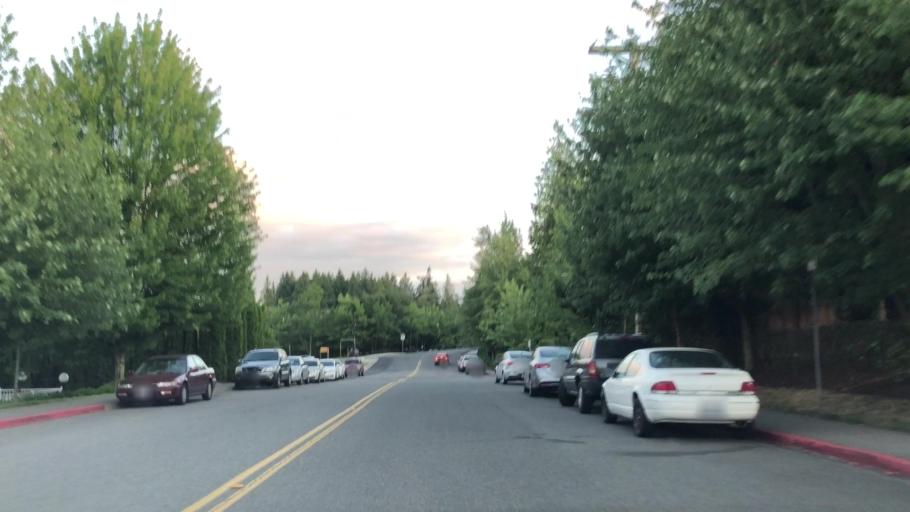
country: US
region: Washington
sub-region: Snohomish County
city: Martha Lake
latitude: 47.8655
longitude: -122.2727
